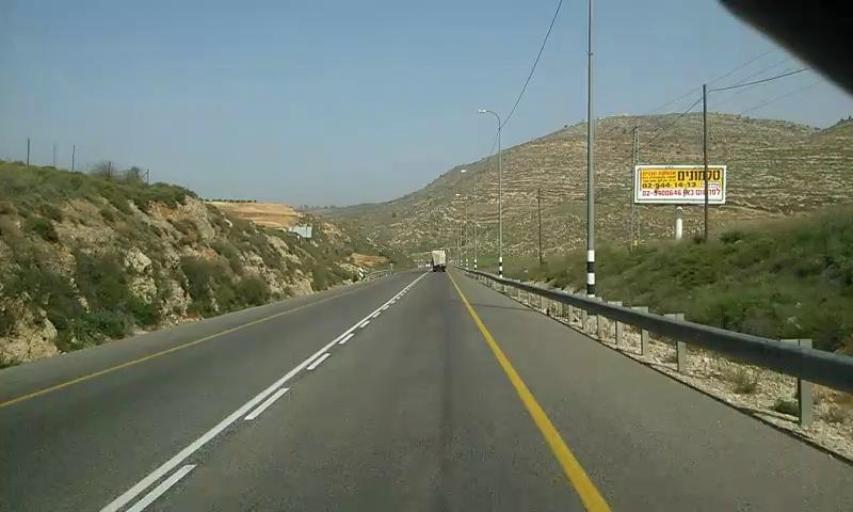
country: PS
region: West Bank
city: Qaryut
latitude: 32.0588
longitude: 35.2843
